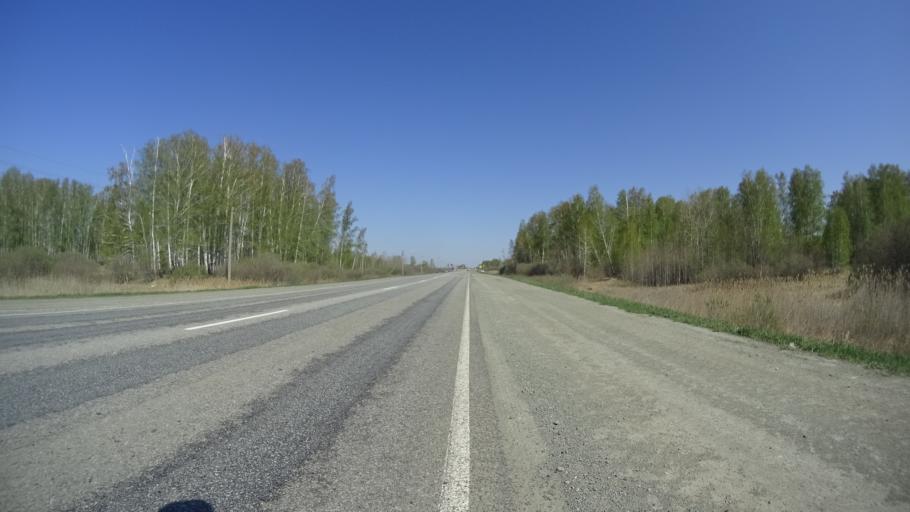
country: RU
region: Chelyabinsk
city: Troitsk
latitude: 54.1838
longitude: 61.4344
